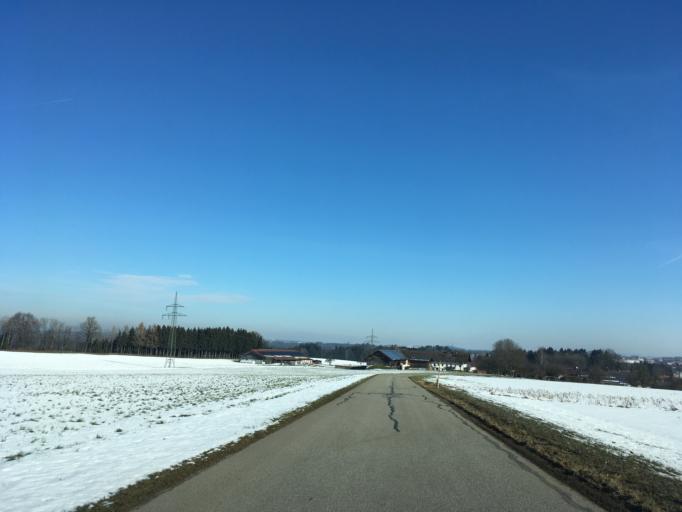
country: DE
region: Bavaria
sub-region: Upper Bavaria
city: Vogtareuth
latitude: 47.9269
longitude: 12.1603
